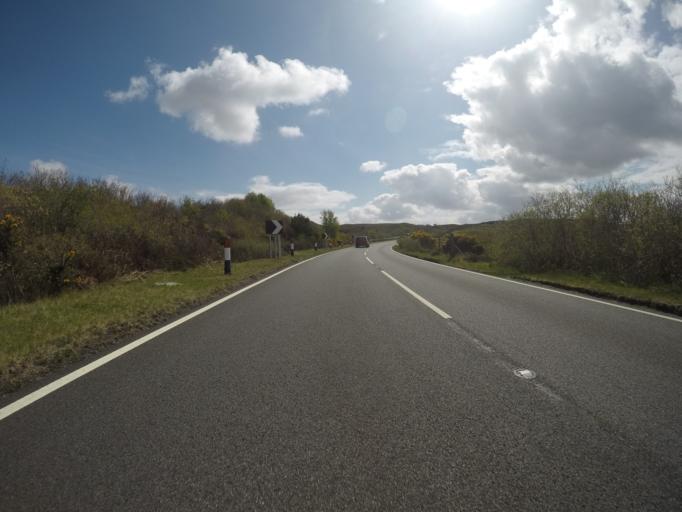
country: GB
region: Scotland
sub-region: Highland
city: Portree
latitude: 57.5205
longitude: -6.3410
